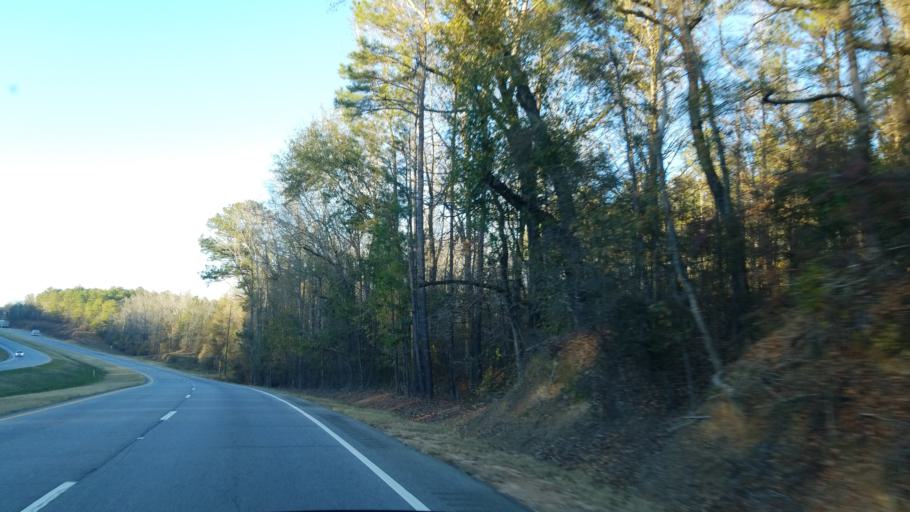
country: US
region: Georgia
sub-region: Chattahoochee County
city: Cusseta
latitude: 32.2508
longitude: -84.7203
